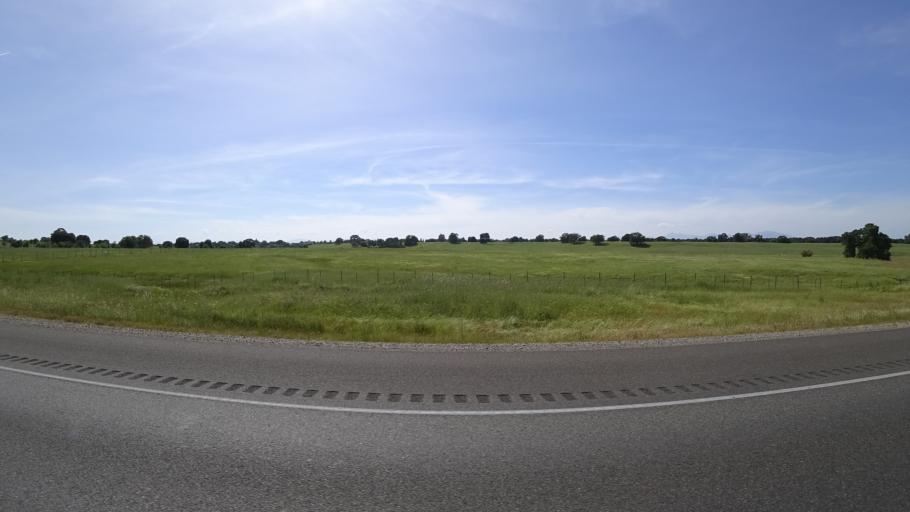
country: US
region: California
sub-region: Shasta County
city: Cottonwood
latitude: 40.3523
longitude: -122.2832
